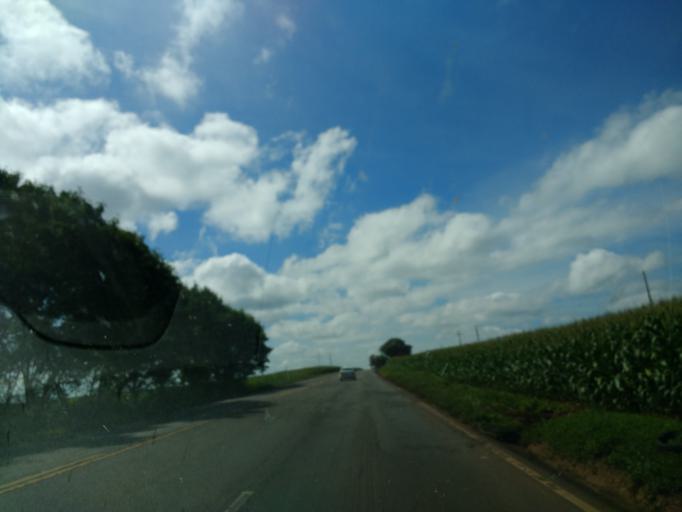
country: BR
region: Parana
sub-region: Cianorte
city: Cianorte
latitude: -23.6480
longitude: -52.4877
